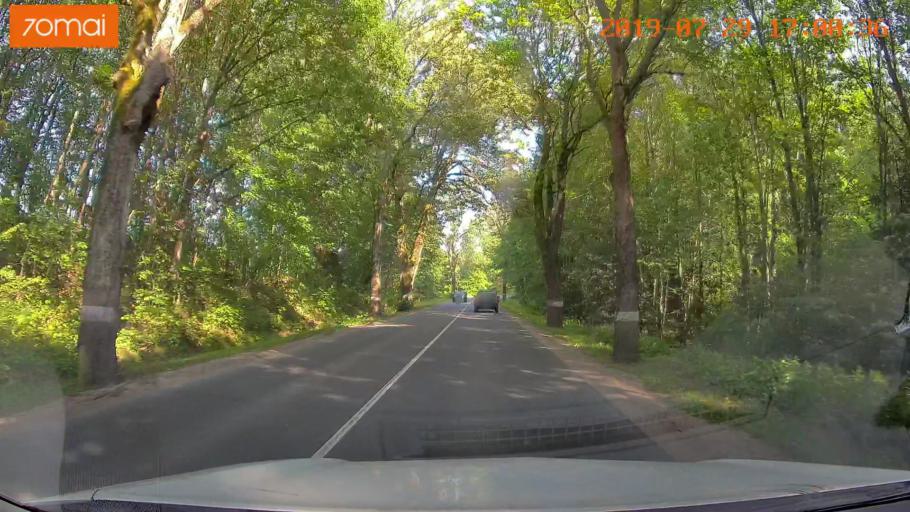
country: RU
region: Kaliningrad
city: Volochayevskoye
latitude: 54.8189
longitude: 20.2284
